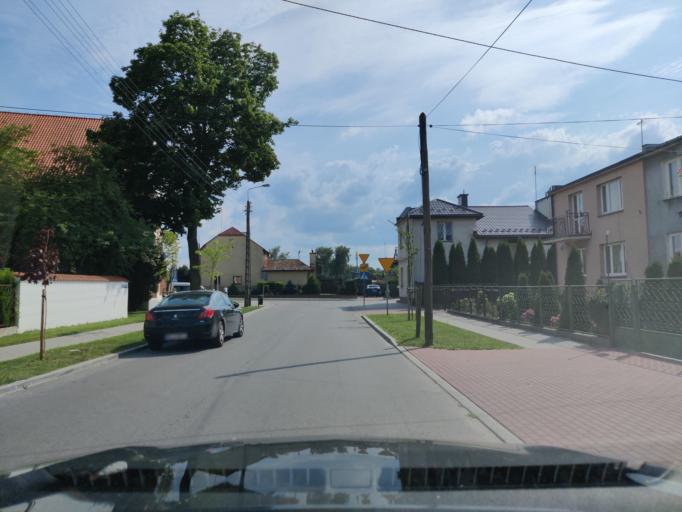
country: PL
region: Masovian Voivodeship
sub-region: Powiat pultuski
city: Pultusk
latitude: 52.7014
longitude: 21.0888
